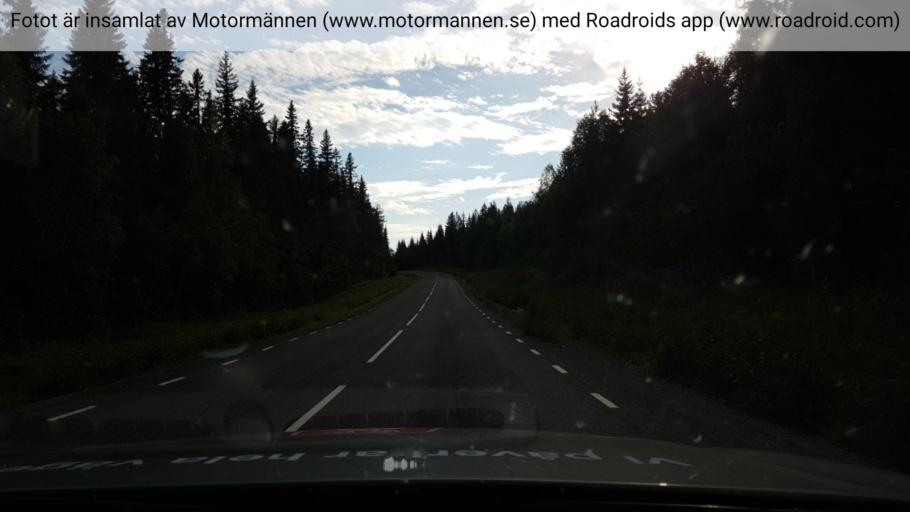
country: SE
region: Jaemtland
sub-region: Ragunda Kommun
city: Hammarstrand
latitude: 63.5543
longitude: 16.1088
